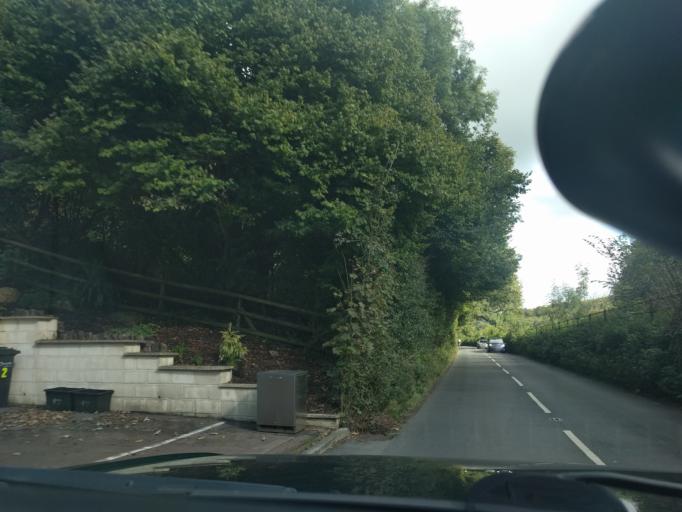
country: GB
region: England
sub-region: Bath and North East Somerset
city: Freshford
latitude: 51.3529
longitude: -2.3138
